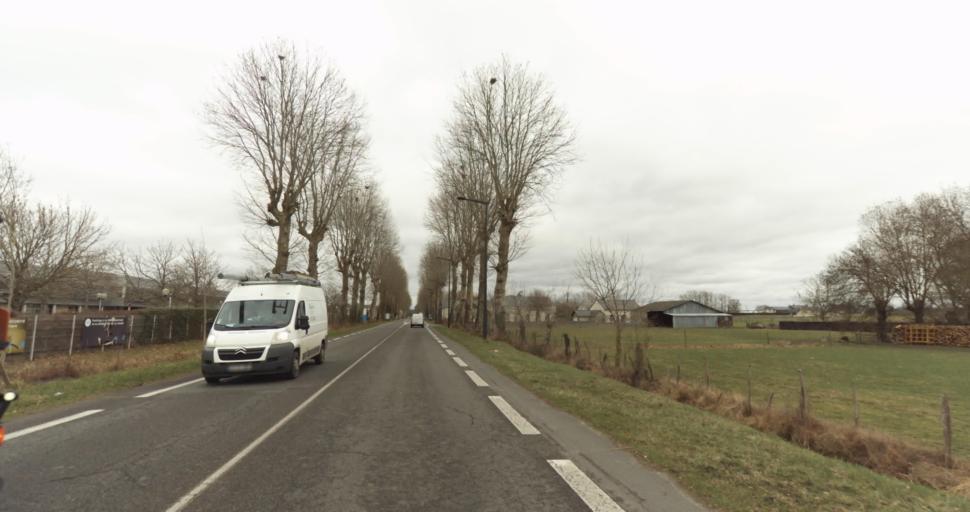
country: FR
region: Pays de la Loire
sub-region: Departement de Maine-et-Loire
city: Saumur
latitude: 47.2815
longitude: -0.0534
